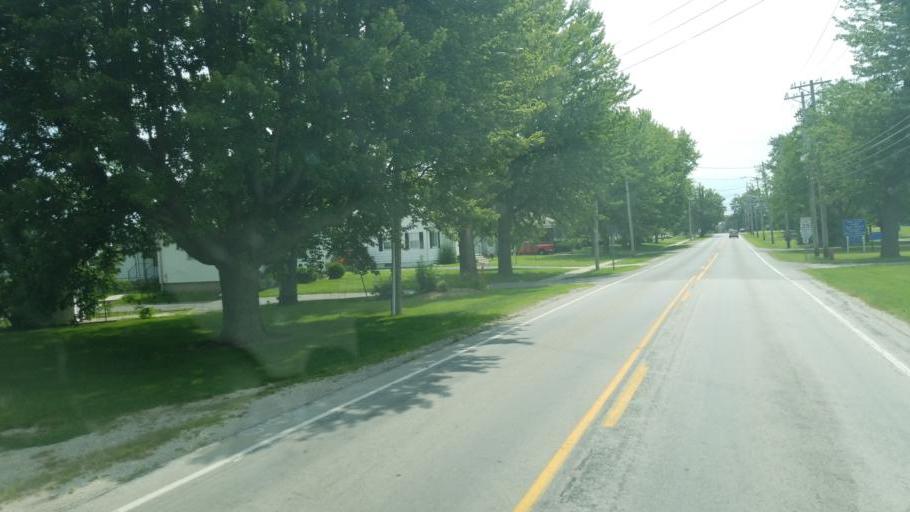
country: US
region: Ohio
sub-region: Wyandot County
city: Carey
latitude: 40.9561
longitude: -83.3967
